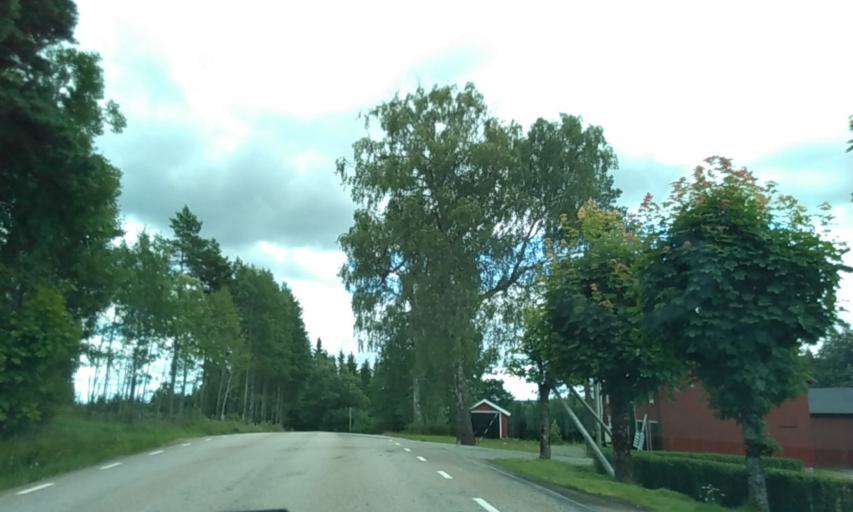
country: SE
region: Vaestra Goetaland
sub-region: Boras Kommun
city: Boras
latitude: 57.8106
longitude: 12.9561
